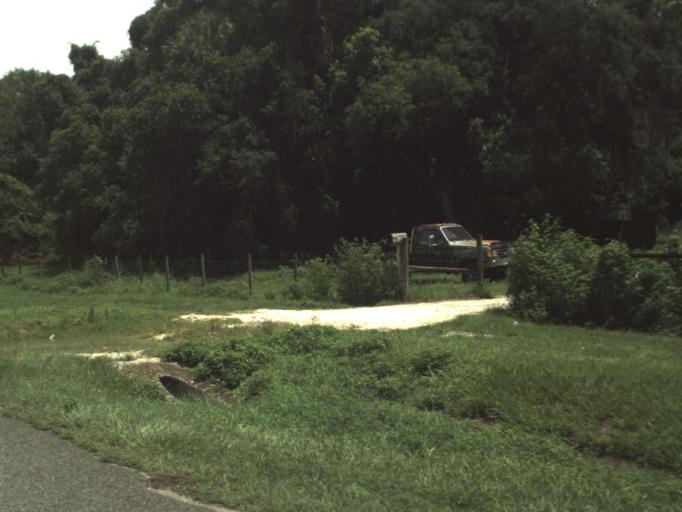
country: US
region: Florida
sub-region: Sumter County
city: Lake Panasoffkee
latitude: 28.7738
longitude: -82.0657
